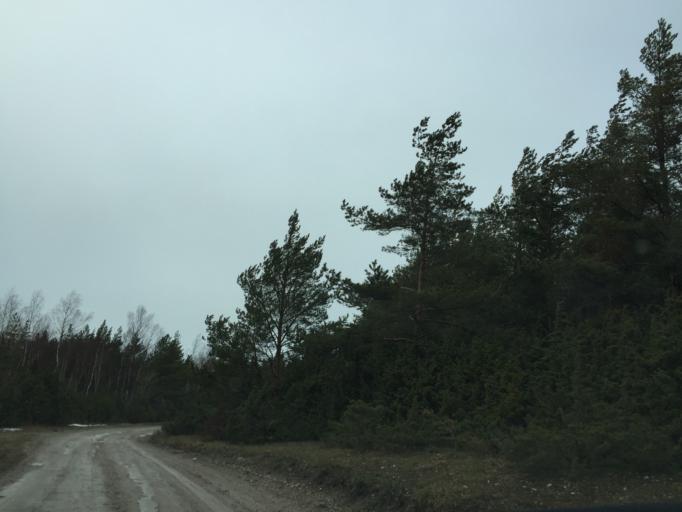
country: EE
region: Saare
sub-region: Kuressaare linn
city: Kuressaare
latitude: 58.4999
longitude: 21.9218
